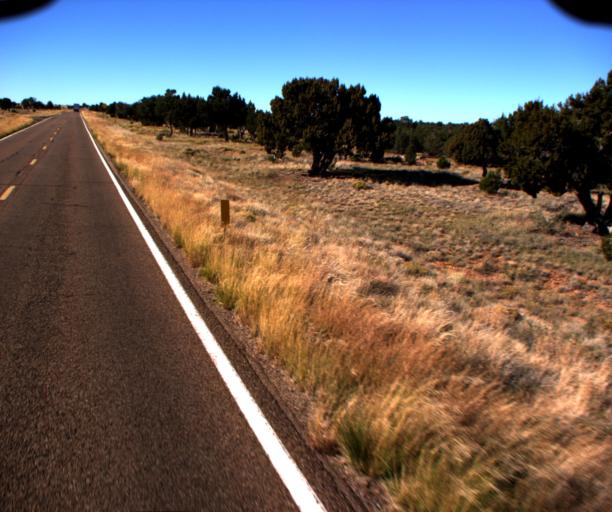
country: US
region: Arizona
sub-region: Navajo County
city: Heber-Overgaard
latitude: 34.4777
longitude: -110.4662
